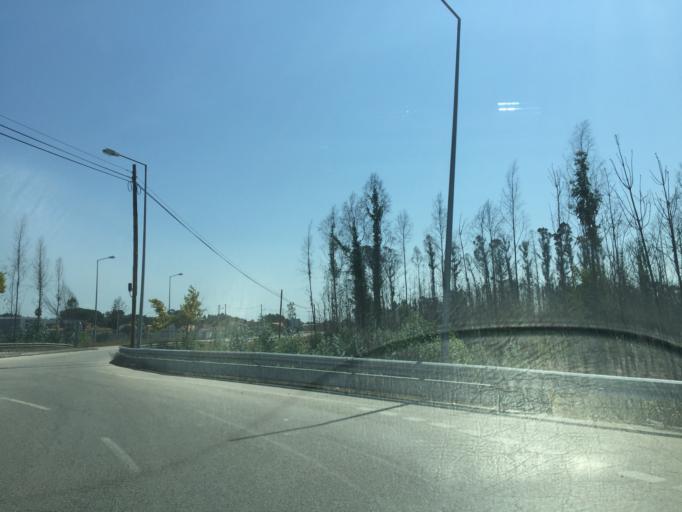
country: PT
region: Coimbra
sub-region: Mira
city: Mira
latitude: 40.3366
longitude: -8.7506
